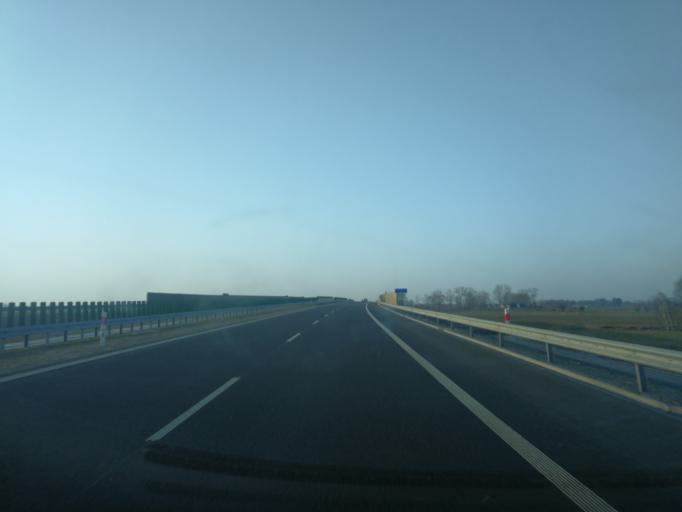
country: PL
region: Pomeranian Voivodeship
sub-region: Powiat nowodworski
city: Nowy Dwor Gdanski
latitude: 54.1790
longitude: 19.1839
